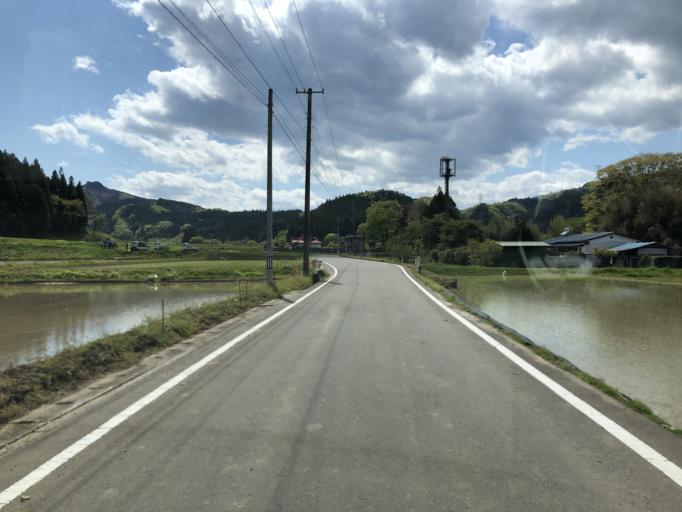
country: JP
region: Fukushima
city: Ishikawa
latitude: 37.0078
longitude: 140.3357
